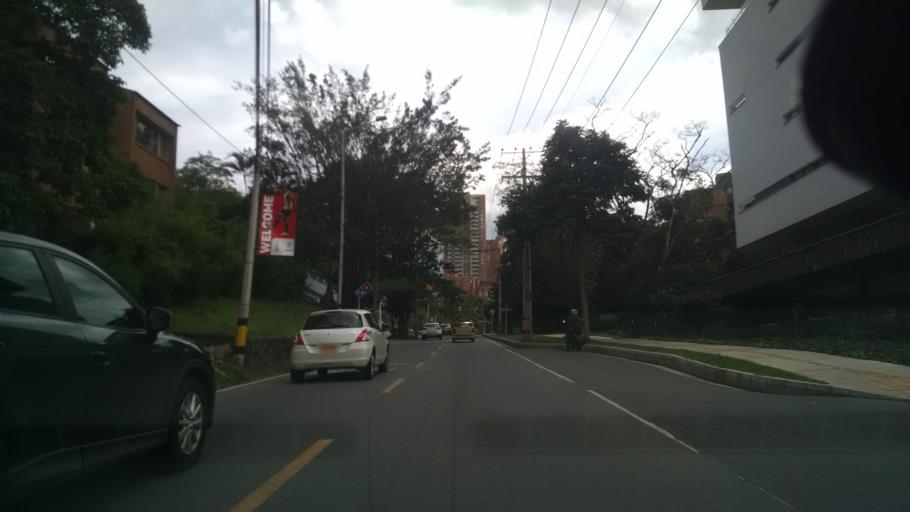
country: CO
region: Antioquia
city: Medellin
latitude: 6.2117
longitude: -75.5591
